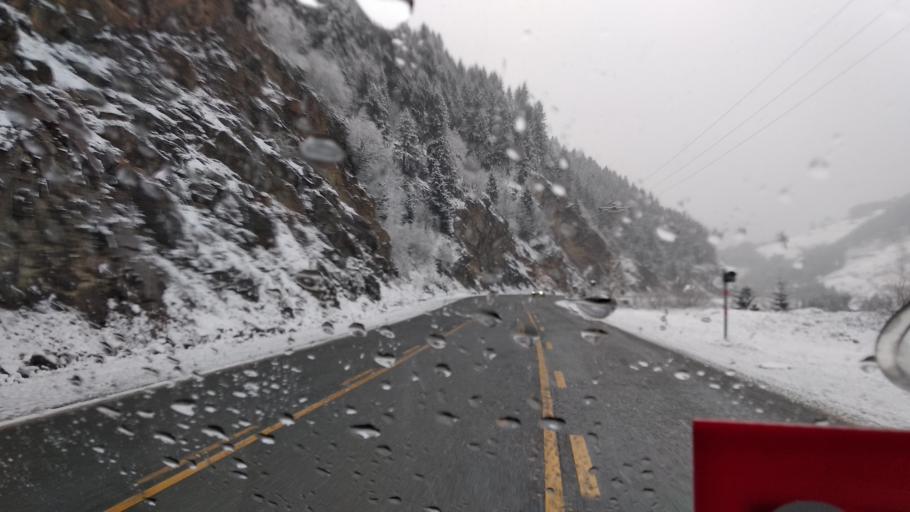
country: TR
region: Gumushane
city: Yaglidere
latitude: 40.6808
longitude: 39.4458
